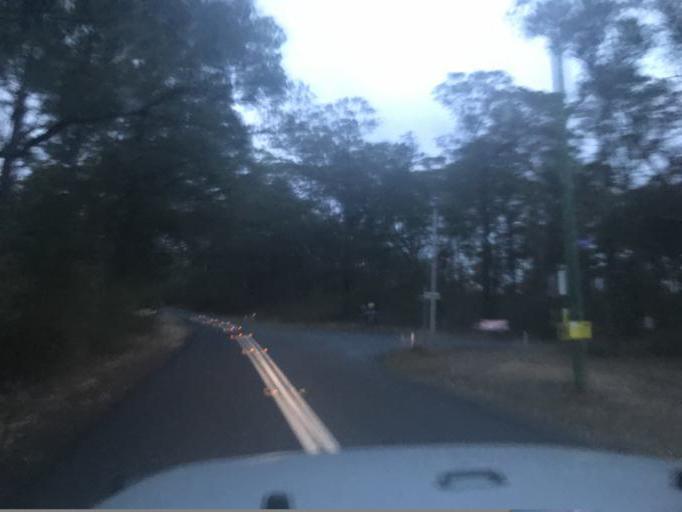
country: AU
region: New South Wales
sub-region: Hawkesbury
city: Pitt Town
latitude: -33.4730
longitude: 150.8667
